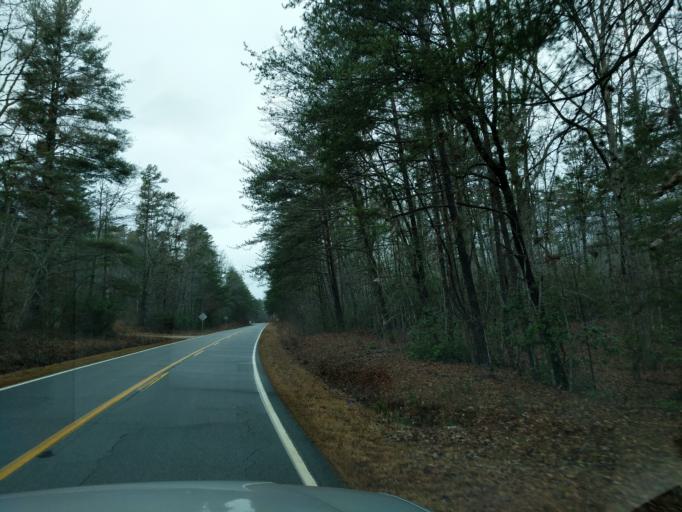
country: US
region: South Carolina
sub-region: Oconee County
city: Walhalla
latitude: 34.7883
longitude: -83.1855
